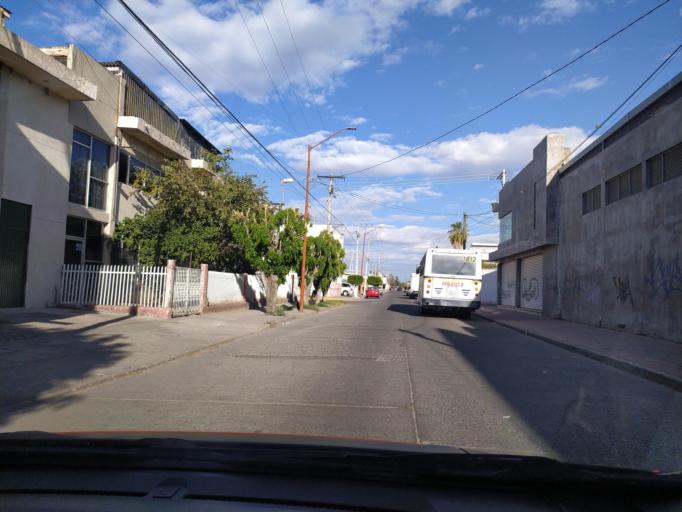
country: MX
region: Guanajuato
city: San Francisco del Rincon
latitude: 21.0260
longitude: -101.8547
